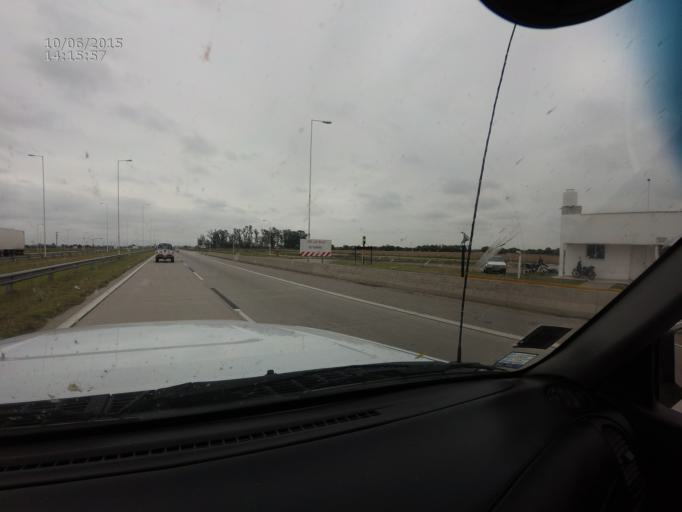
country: AR
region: Cordoba
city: Villa Maria
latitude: -32.4048
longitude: -63.1849
